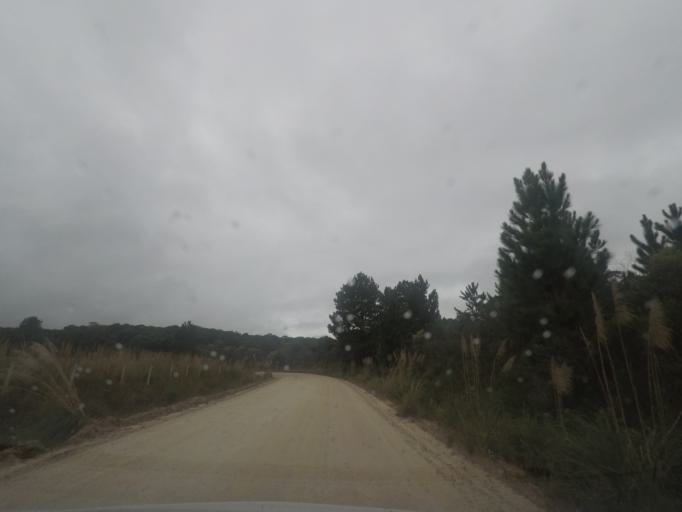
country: BR
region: Parana
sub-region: Campina Grande Do Sul
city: Campina Grande do Sul
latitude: -25.3104
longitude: -49.0947
